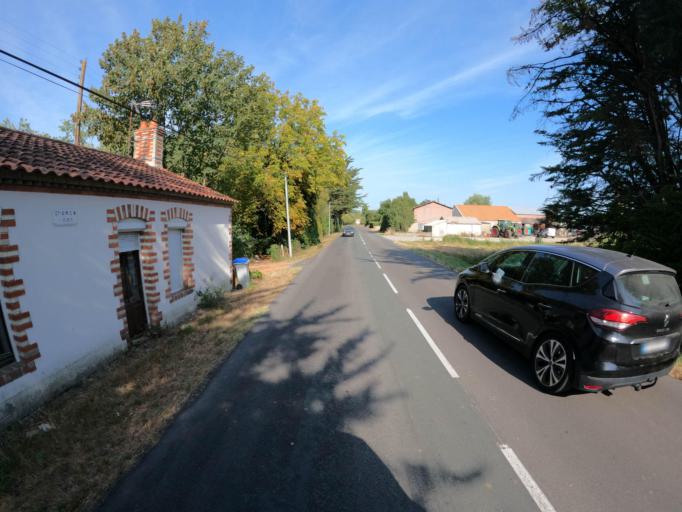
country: FR
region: Pays de la Loire
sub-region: Departement de la Vendee
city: Le Perrier
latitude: 46.8054
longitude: -1.9734
